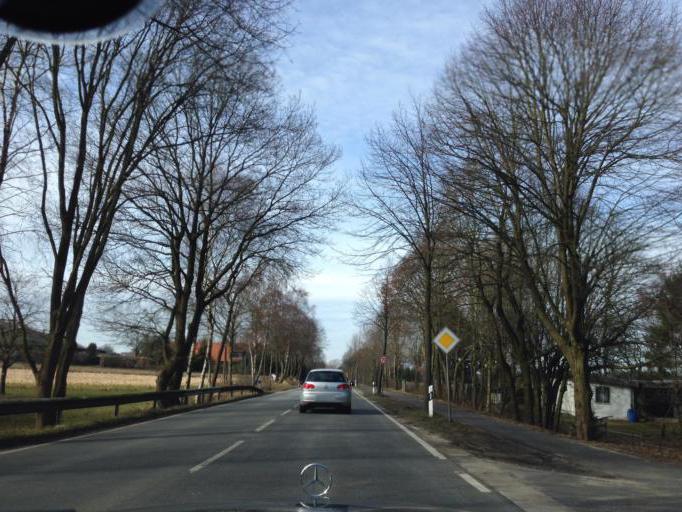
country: DE
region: Lower Saxony
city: Seevetal
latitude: 53.4382
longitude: 9.9127
